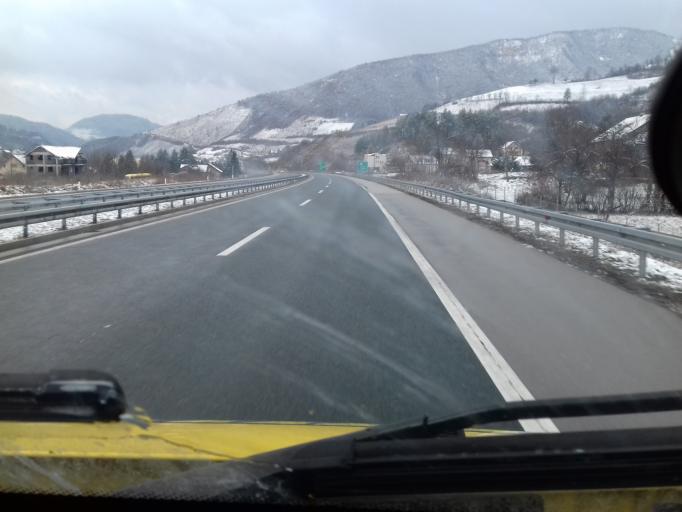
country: BA
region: Federation of Bosnia and Herzegovina
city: Kacuni
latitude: 44.1351
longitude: 18.0024
